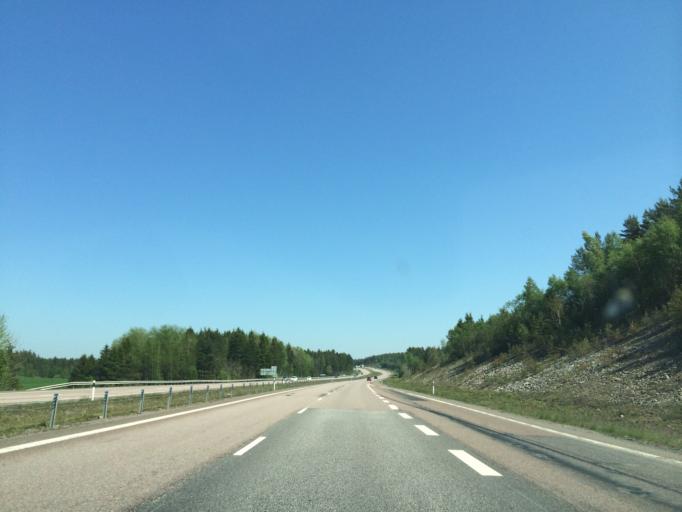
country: SE
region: Soedermanland
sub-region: Nykopings Kommun
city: Olstorp
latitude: 58.7561
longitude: 16.6267
